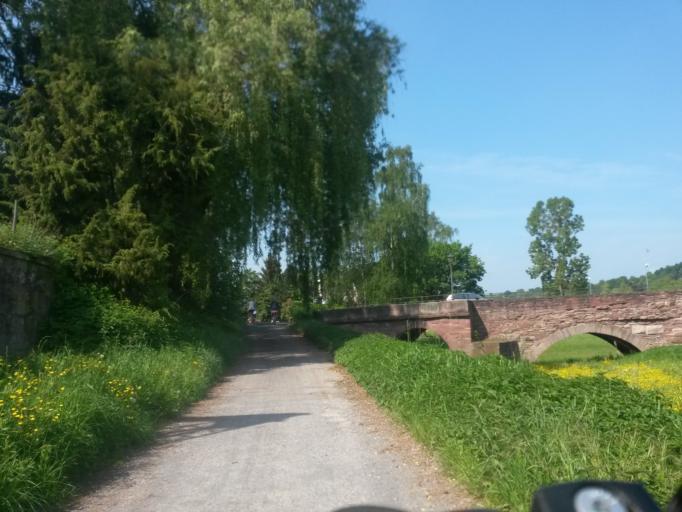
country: DE
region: Bavaria
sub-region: Regierungsbezirk Unterfranken
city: Euerdorf
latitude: 50.1507
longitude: 10.0275
